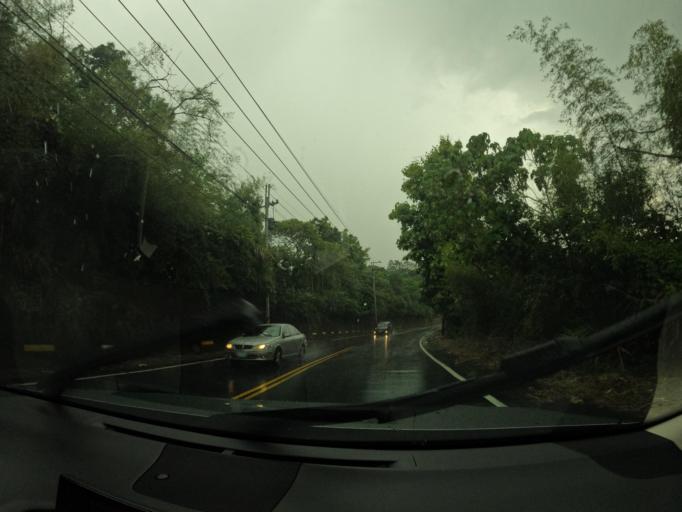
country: TW
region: Taiwan
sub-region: Nantou
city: Nantou
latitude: 23.8853
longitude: 120.7442
